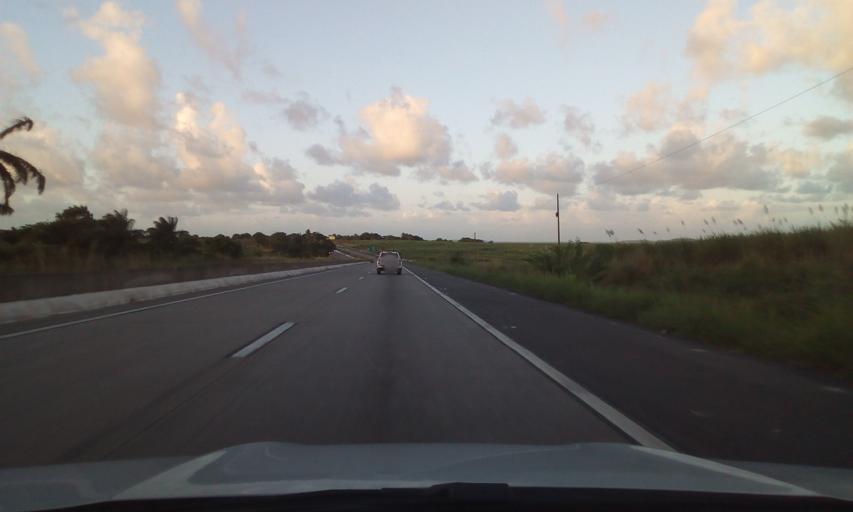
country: BR
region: Pernambuco
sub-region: Itapissuma
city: Itapissuma
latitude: -7.7105
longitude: -34.9303
